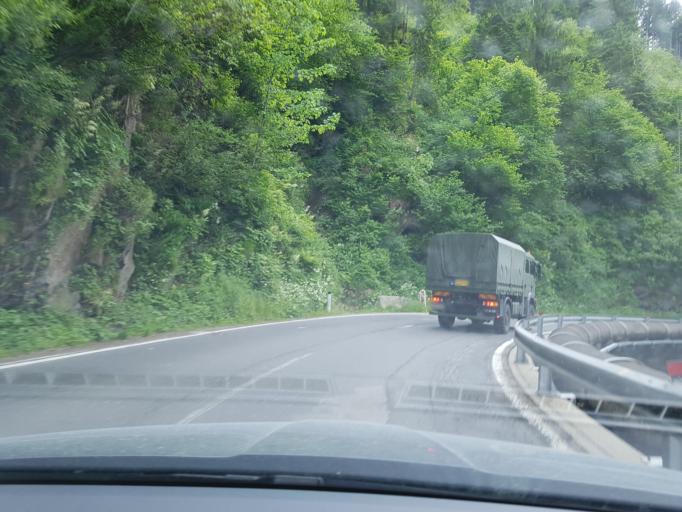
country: AT
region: Carinthia
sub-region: Politischer Bezirk Villach Land
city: Feld am See
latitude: 46.8003
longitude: 13.7523
